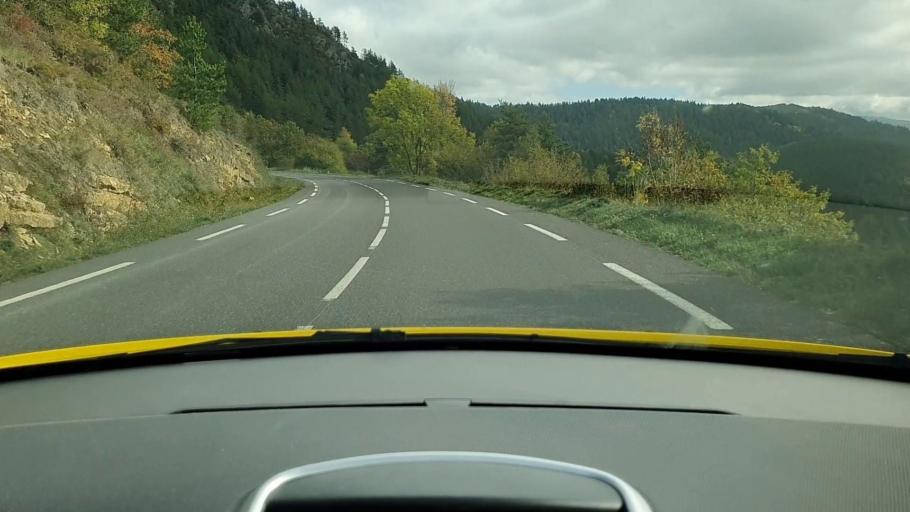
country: FR
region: Languedoc-Roussillon
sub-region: Departement de la Lozere
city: Meyrueis
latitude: 44.1276
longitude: 3.4104
